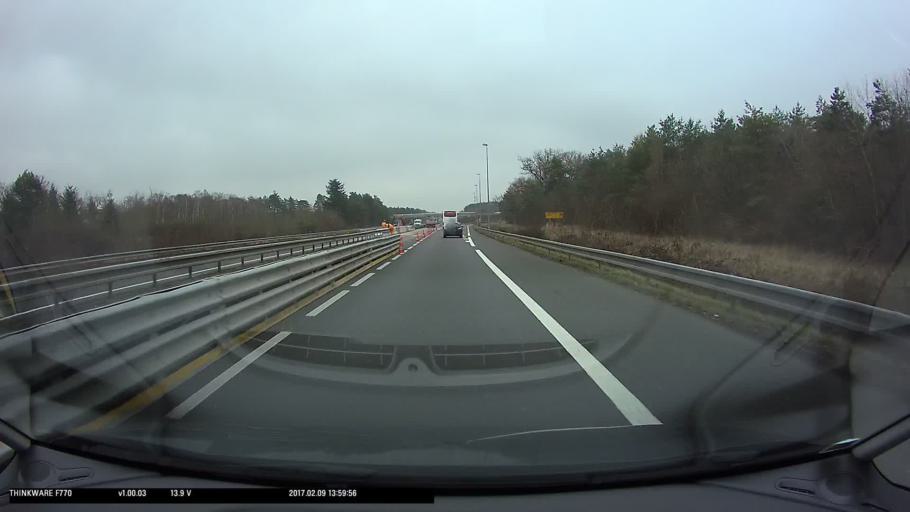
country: FR
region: Centre
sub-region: Departement du Loir-et-Cher
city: Lamotte-Beuvron
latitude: 47.5844
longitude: 1.9929
